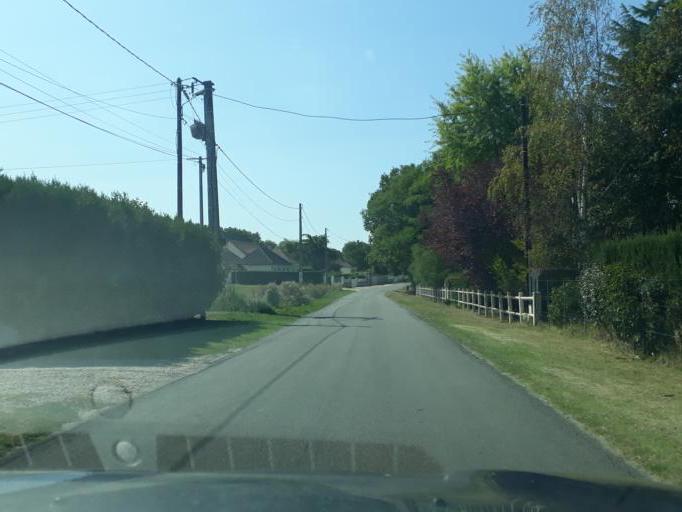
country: FR
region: Centre
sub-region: Departement de l'Indre
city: Chabris
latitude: 47.2565
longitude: 1.6739
